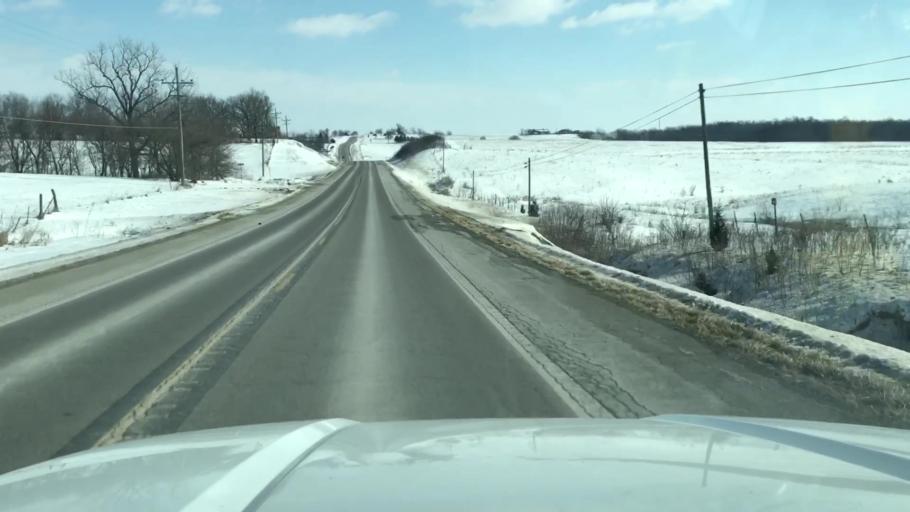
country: US
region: Missouri
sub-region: Nodaway County
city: Maryville
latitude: 40.3445
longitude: -94.7867
